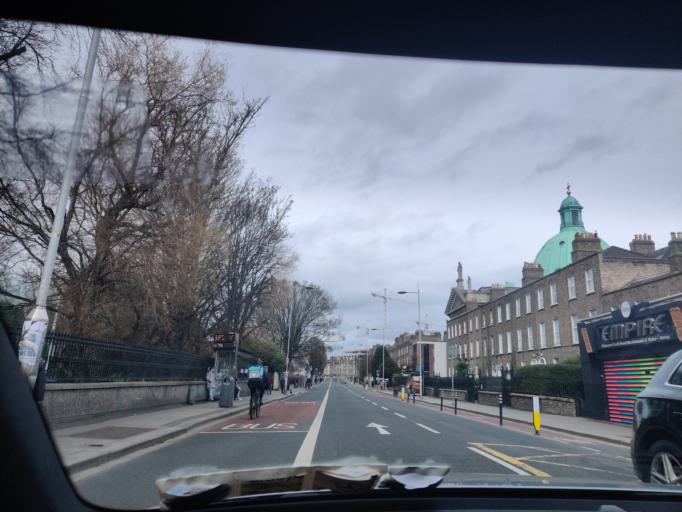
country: IE
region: Leinster
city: Rathmines
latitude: 53.3270
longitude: -6.2648
